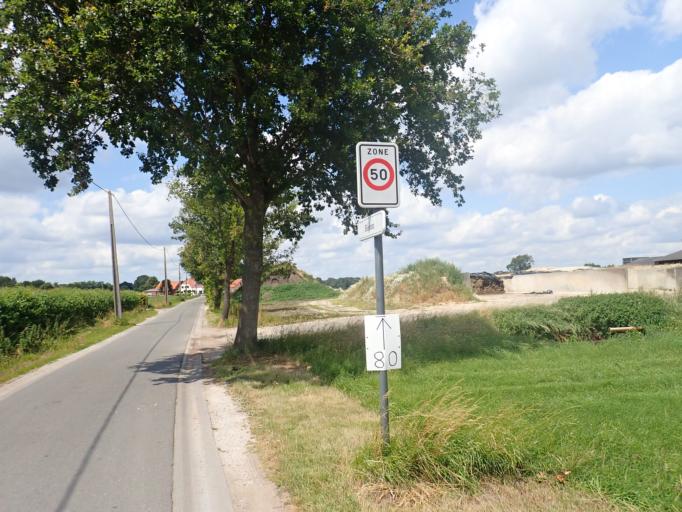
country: BE
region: Flanders
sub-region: Provincie Antwerpen
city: Wuustwezel
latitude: 51.3783
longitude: 4.5568
